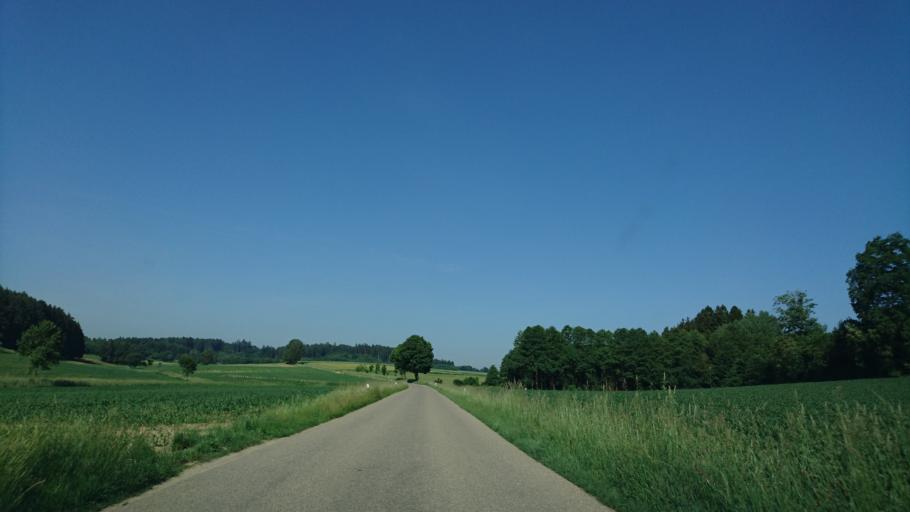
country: DE
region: Bavaria
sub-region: Swabia
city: Gessertshausen
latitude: 48.3577
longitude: 10.7336
